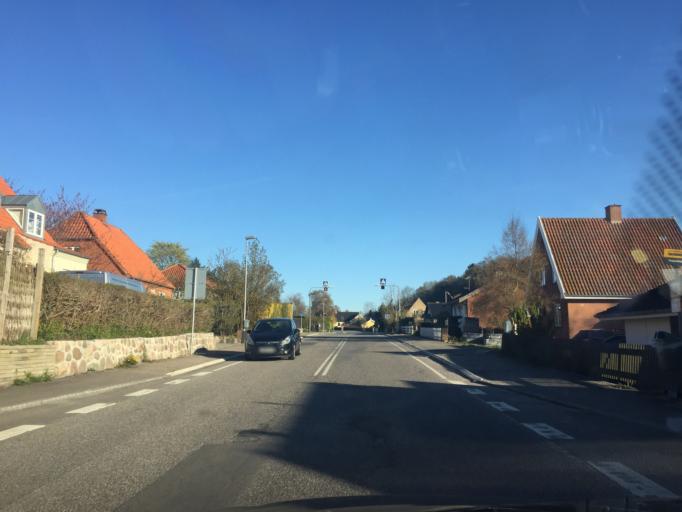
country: DK
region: Capital Region
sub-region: Halsnaes Kommune
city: Frederiksvaerk
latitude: 55.9538
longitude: 12.0251
